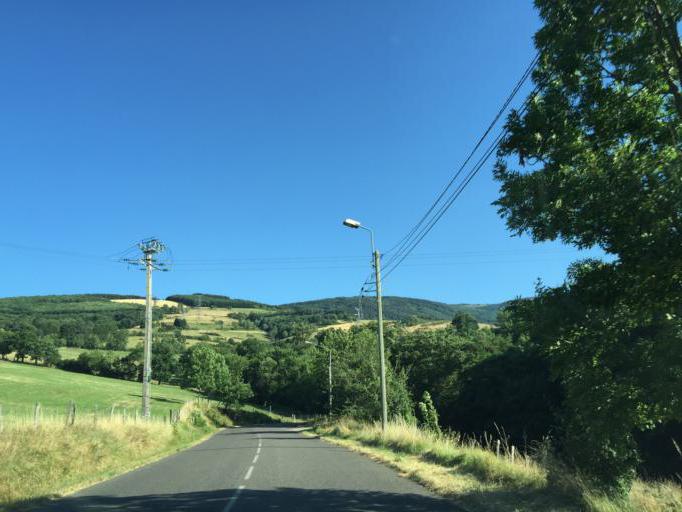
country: FR
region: Rhone-Alpes
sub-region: Departement de la Loire
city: Saint-Jean-Bonnefonds
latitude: 45.4502
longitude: 4.4851
